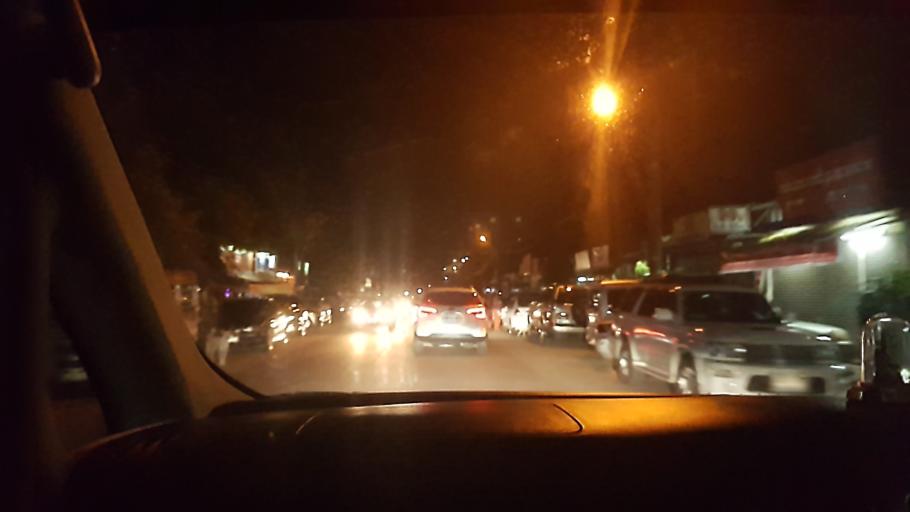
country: MM
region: Yangon
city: Yangon
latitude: 16.8187
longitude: 96.1291
